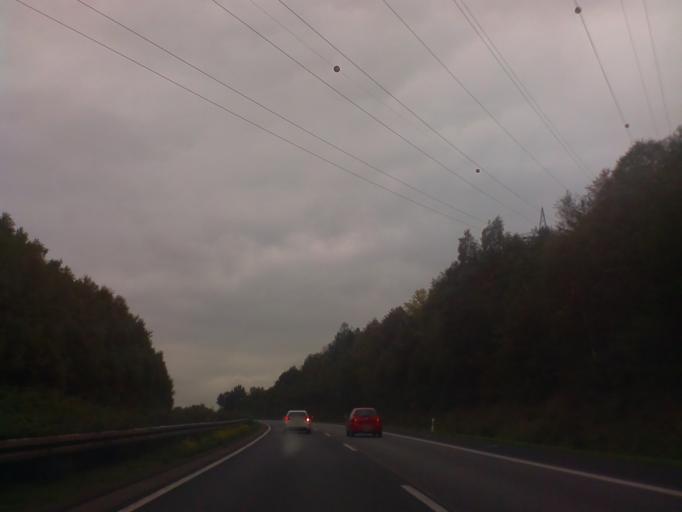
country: DE
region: Hesse
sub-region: Regierungsbezirk Darmstadt
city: Bad Orb
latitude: 50.2505
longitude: 9.3335
